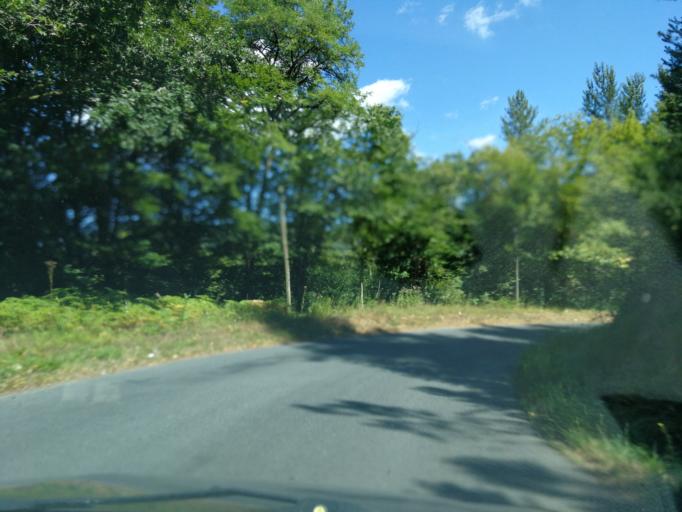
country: FR
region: Limousin
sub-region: Departement de la Correze
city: Argentat
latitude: 45.0953
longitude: 1.9192
